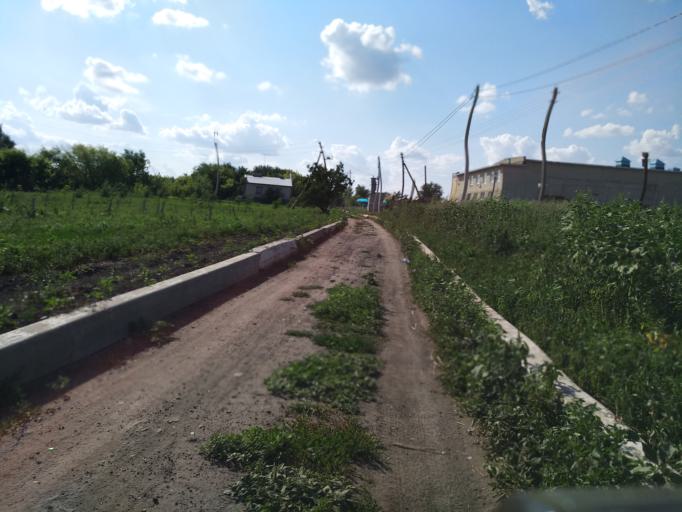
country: RU
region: Lipetsk
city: Dobrinka
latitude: 52.0366
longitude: 40.5564
